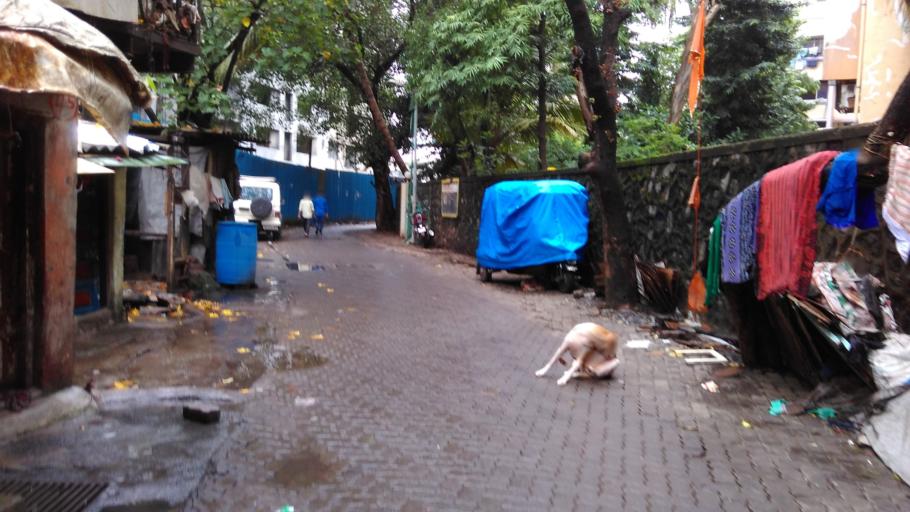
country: IN
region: Maharashtra
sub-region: Mumbai Suburban
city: Mumbai
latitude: 19.0640
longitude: 72.8818
